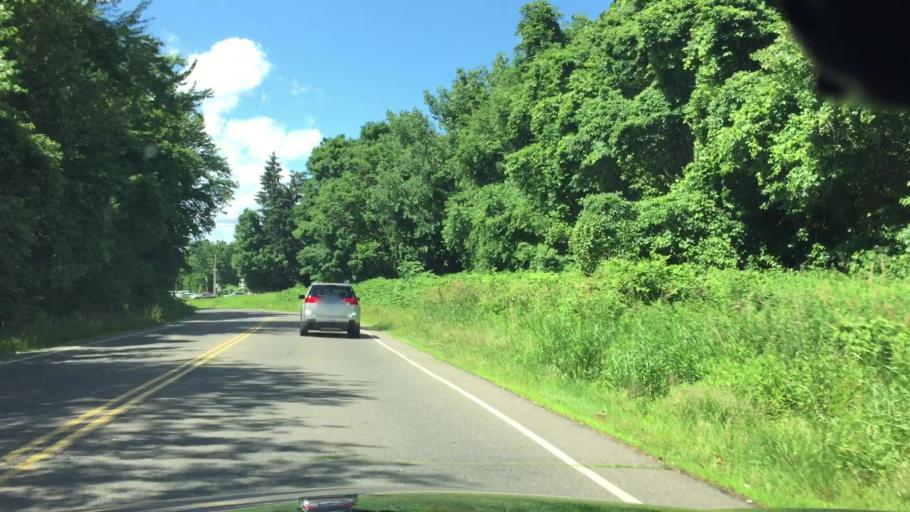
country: US
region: Connecticut
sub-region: New Haven County
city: City of Milford (balance)
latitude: 41.2105
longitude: -73.0792
